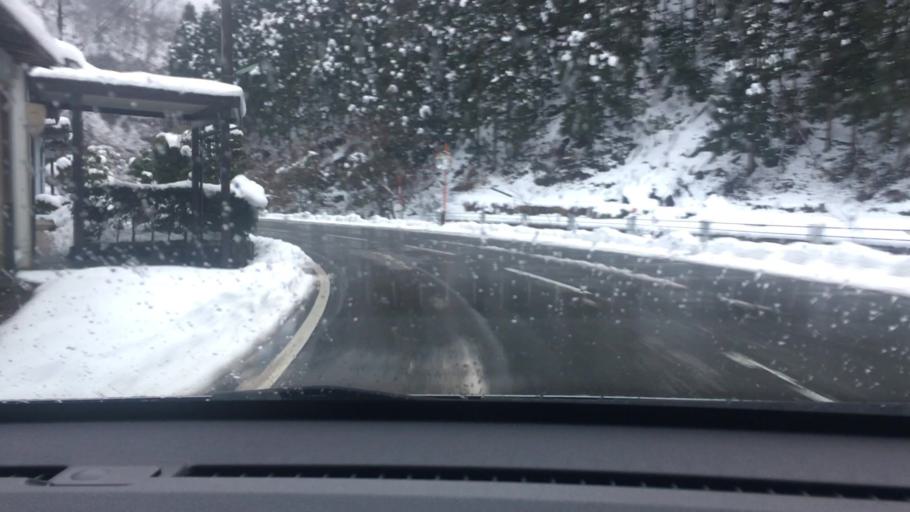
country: JP
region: Hyogo
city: Toyooka
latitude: 35.3690
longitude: 134.5821
